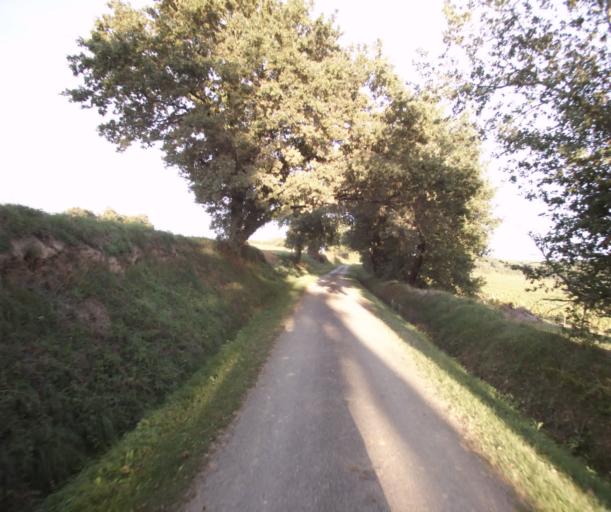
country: FR
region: Midi-Pyrenees
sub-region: Departement du Gers
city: Eauze
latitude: 43.8792
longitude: 0.0114
